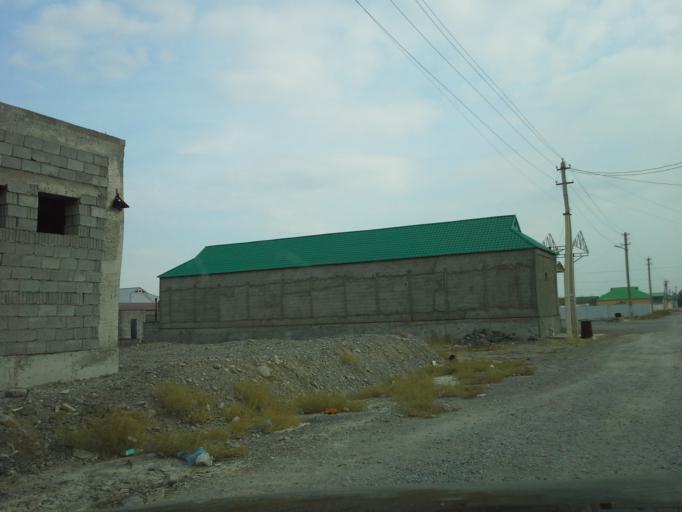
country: TM
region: Ahal
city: Abadan
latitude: 38.0382
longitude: 58.2507
